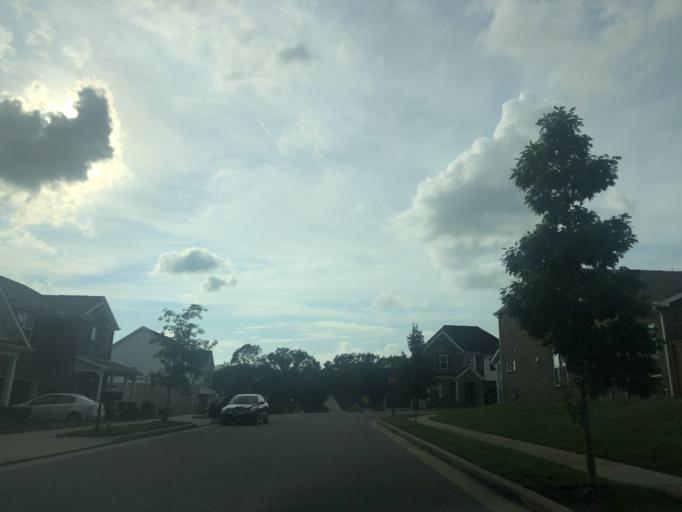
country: US
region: Tennessee
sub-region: Davidson County
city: Lakewood
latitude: 36.1657
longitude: -86.6233
